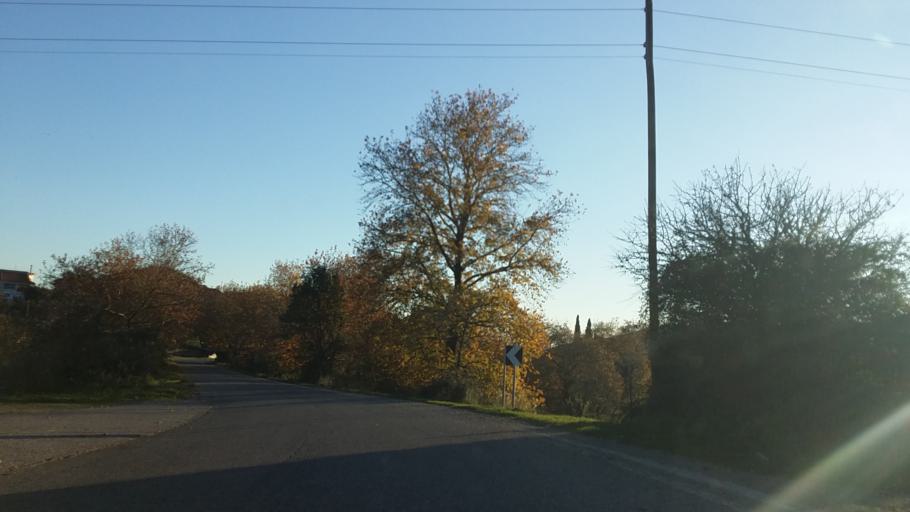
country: GR
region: West Greece
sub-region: Nomos Aitolias kai Akarnanias
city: Lepenou
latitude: 38.7406
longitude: 21.3459
